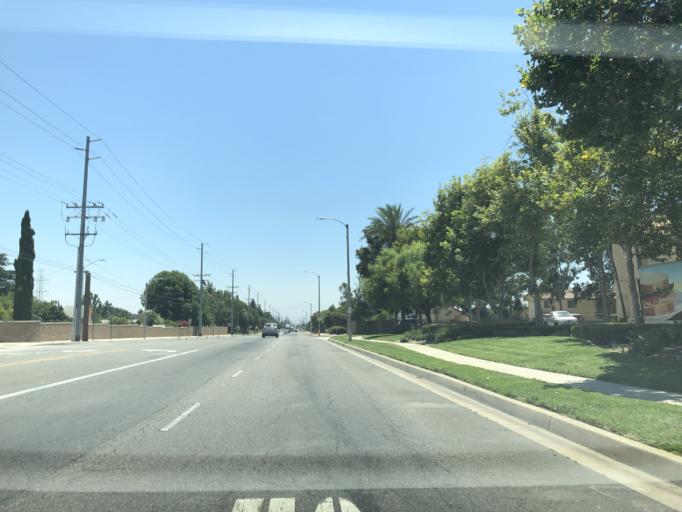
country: US
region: California
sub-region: San Bernardino County
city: Rancho Cucamonga
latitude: 34.1052
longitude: -117.5239
